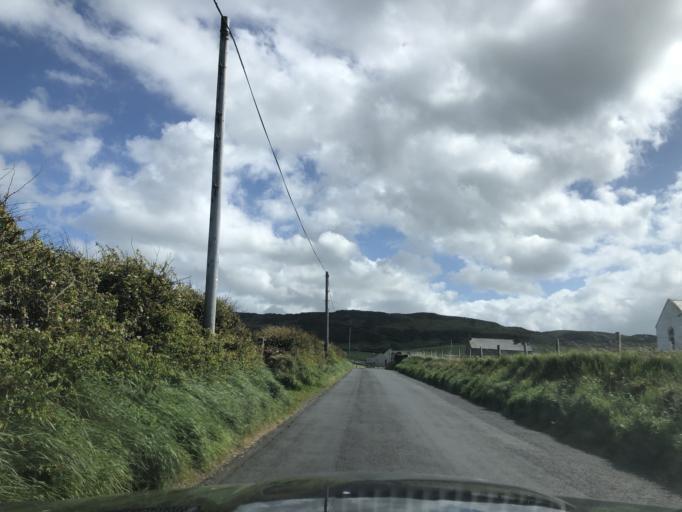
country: GB
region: Northern Ireland
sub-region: Moyle District
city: Ballycastle
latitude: 55.2411
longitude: -6.3663
